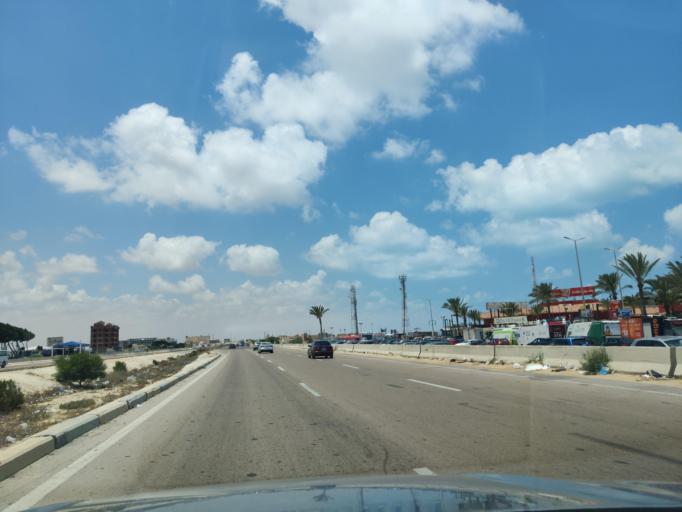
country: EG
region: Muhafazat Matruh
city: Al `Alamayn
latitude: 30.8220
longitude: 29.1738
